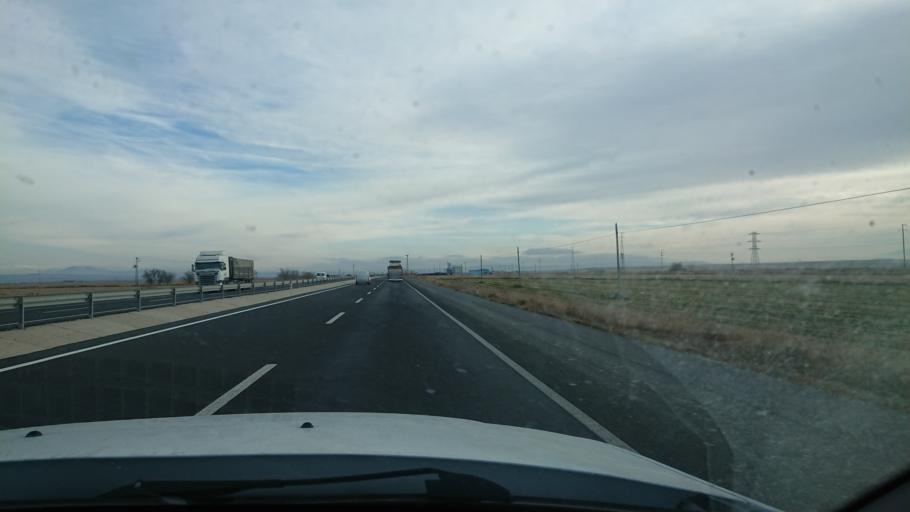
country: TR
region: Aksaray
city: Yesilova
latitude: 38.3153
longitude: 33.8488
